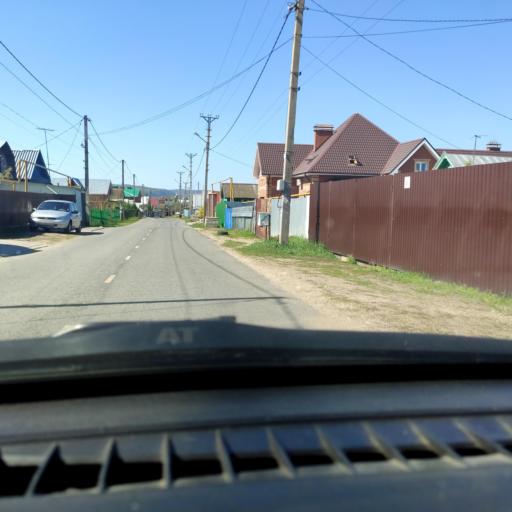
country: RU
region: Samara
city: Zhigulevsk
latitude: 53.4687
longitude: 49.6431
